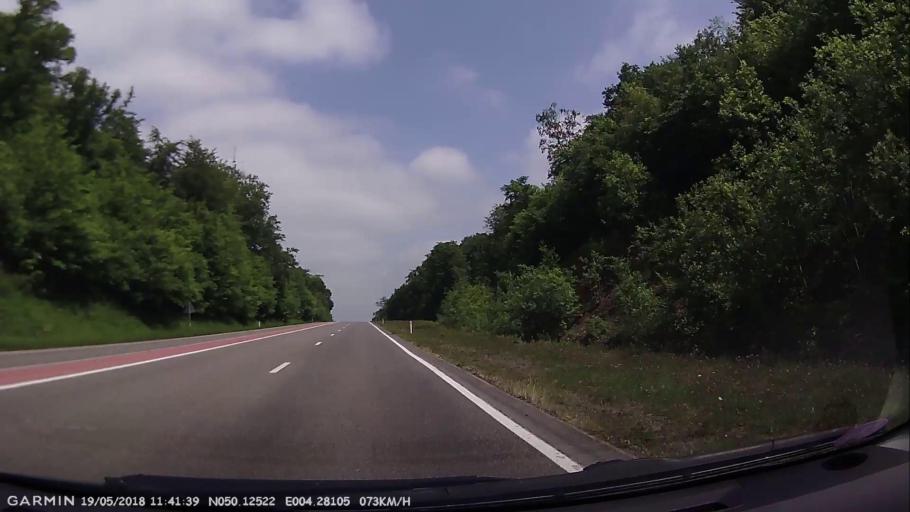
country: BE
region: Wallonia
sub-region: Province du Hainaut
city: Froidchapelle
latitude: 50.1254
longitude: 4.2813
